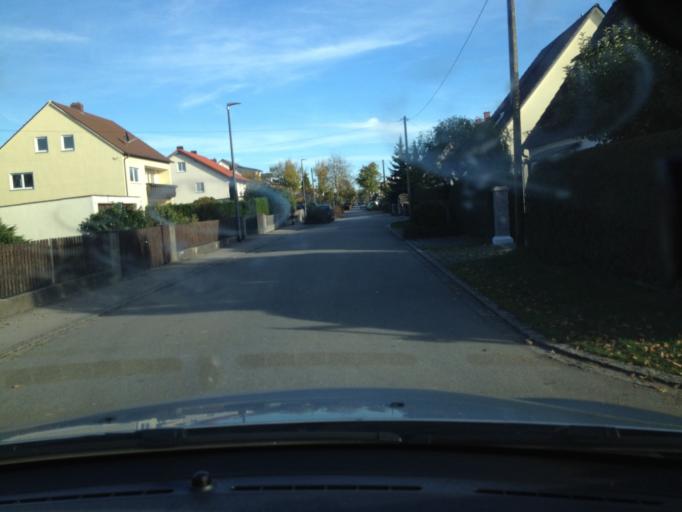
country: DE
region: Bavaria
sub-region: Swabia
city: Oberottmarshausen
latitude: 48.2355
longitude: 10.8566
